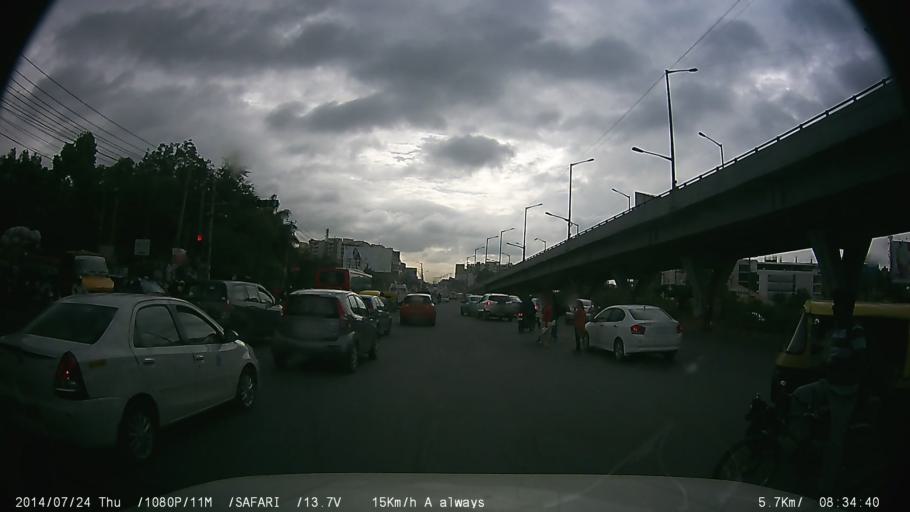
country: IN
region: Karnataka
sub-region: Bangalore Urban
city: Bangalore
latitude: 12.9210
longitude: 77.6651
